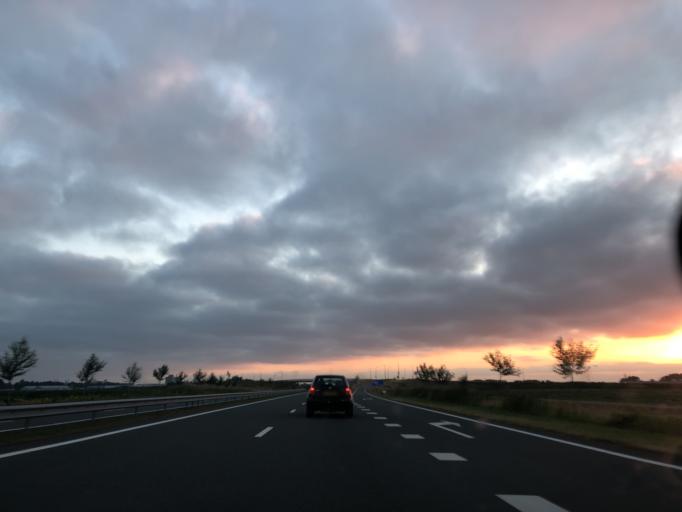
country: NL
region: Groningen
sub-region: Gemeente Veendam
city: Veendam
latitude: 53.0734
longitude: 6.8797
